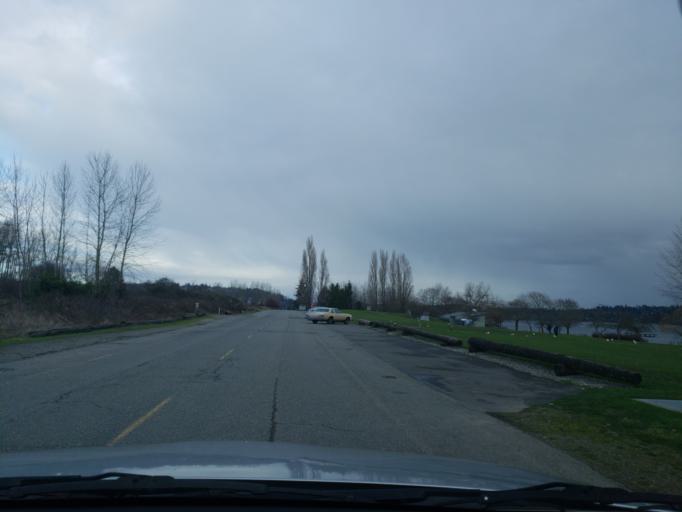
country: US
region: Washington
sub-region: King County
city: Kirkland
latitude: 47.6795
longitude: -122.2490
